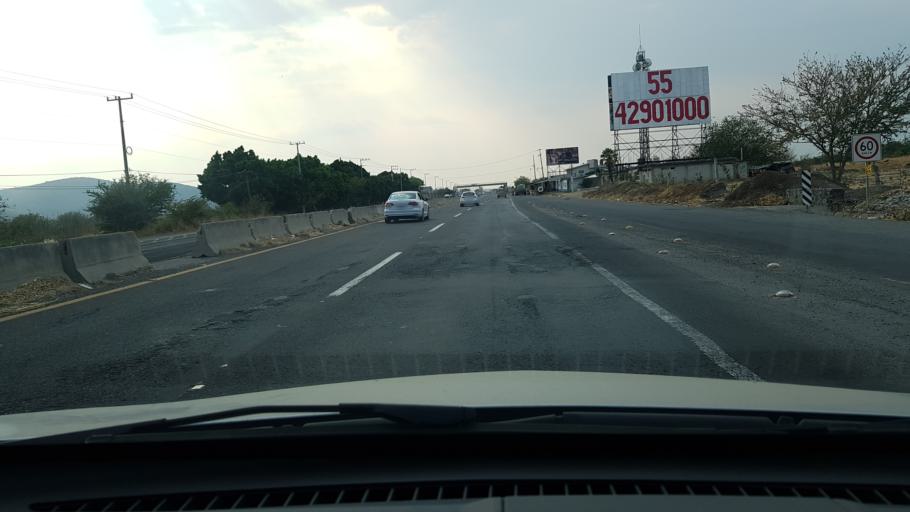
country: MX
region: Morelos
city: Amayuca
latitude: 18.7364
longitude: -98.8225
